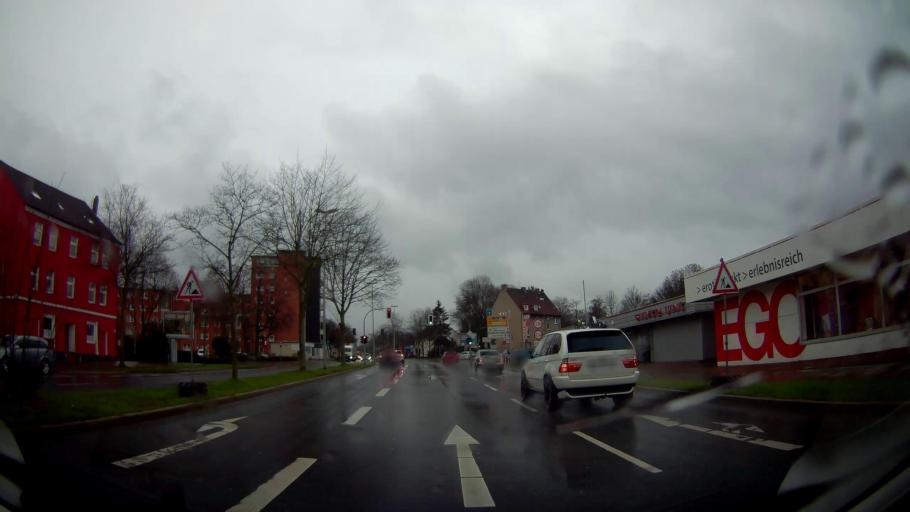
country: DE
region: North Rhine-Westphalia
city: Bochum-Hordel
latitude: 51.5314
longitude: 7.1862
